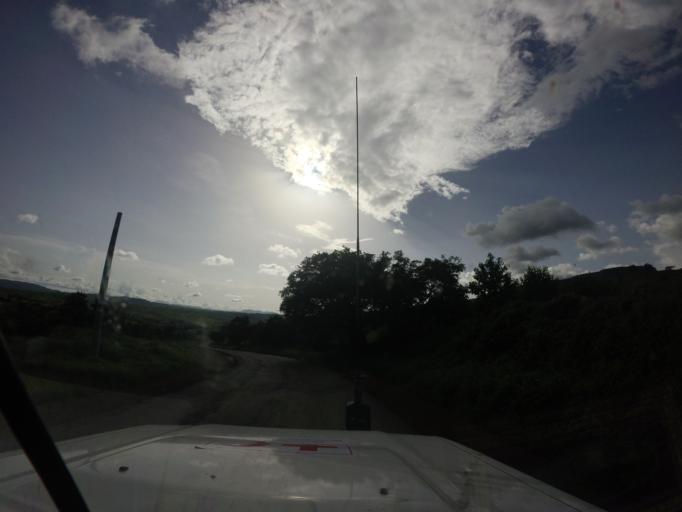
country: GN
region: Kindia
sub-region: Kindia
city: Kindia
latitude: 10.1107
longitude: -12.5511
